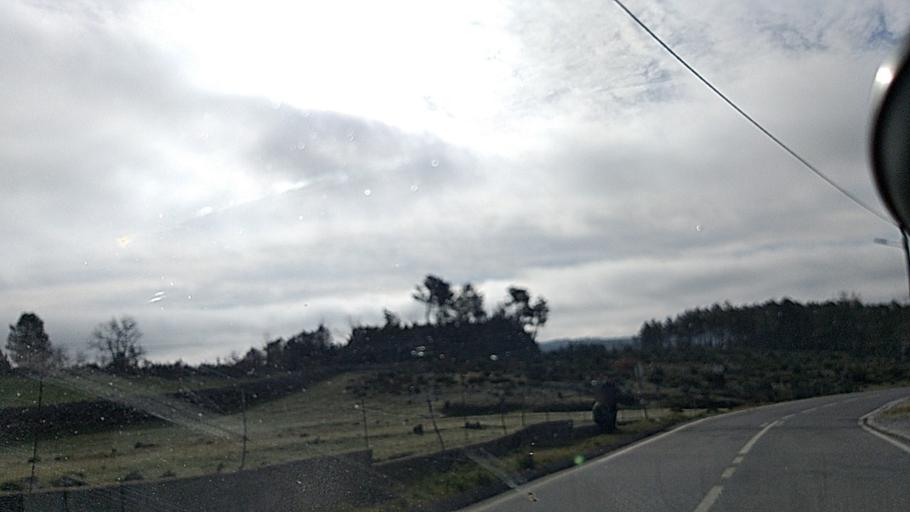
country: PT
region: Guarda
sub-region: Aguiar da Beira
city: Aguiar da Beira
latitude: 40.7800
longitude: -7.5183
